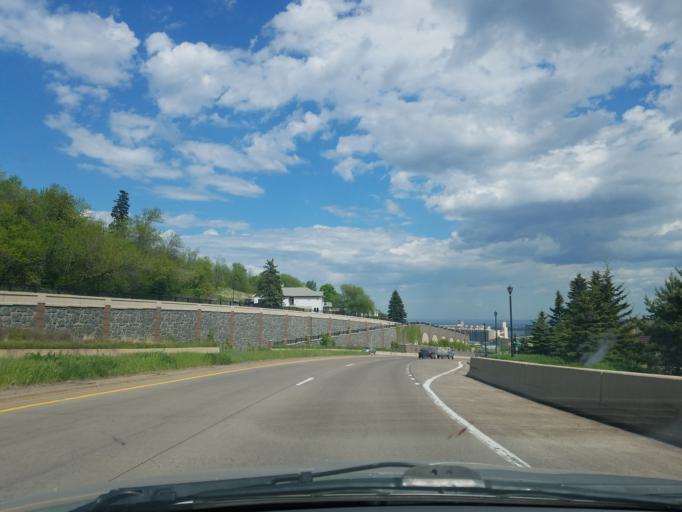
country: US
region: Minnesota
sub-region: Saint Louis County
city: Duluth
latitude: 46.7719
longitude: -92.1331
